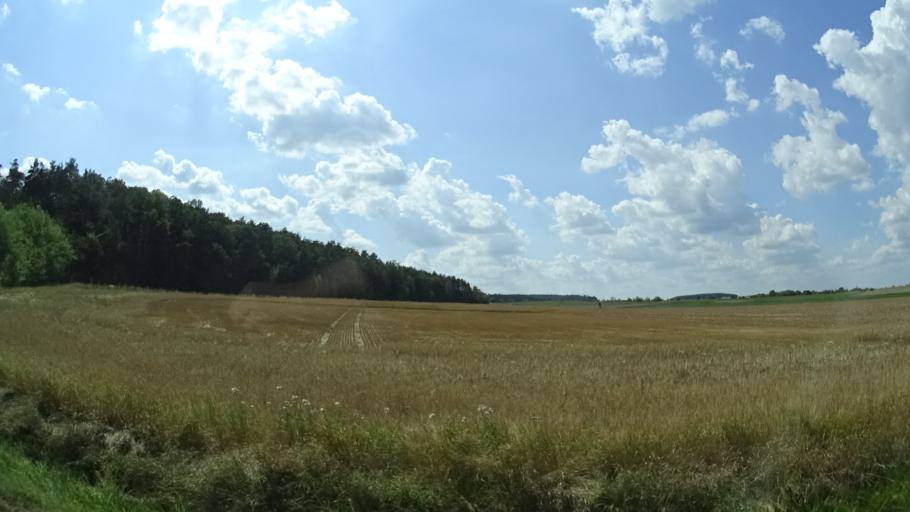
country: DE
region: Bavaria
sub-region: Regierungsbezirk Unterfranken
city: Trappstadt
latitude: 50.3429
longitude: 10.5711
